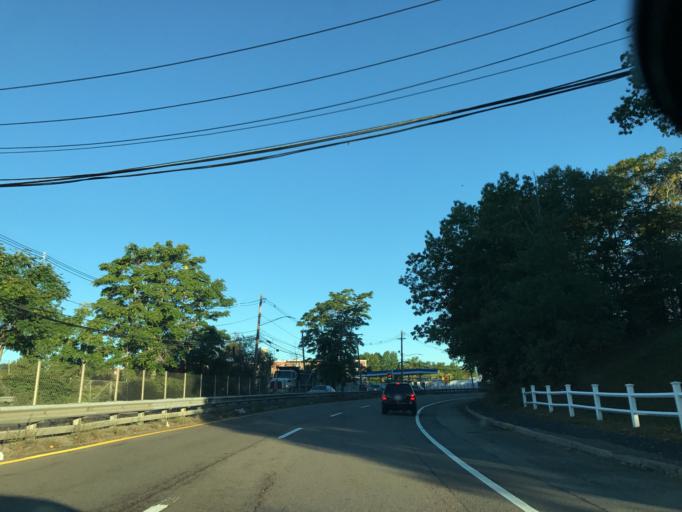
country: US
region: Massachusetts
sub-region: Norfolk County
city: Dedham
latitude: 42.2683
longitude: -71.1714
